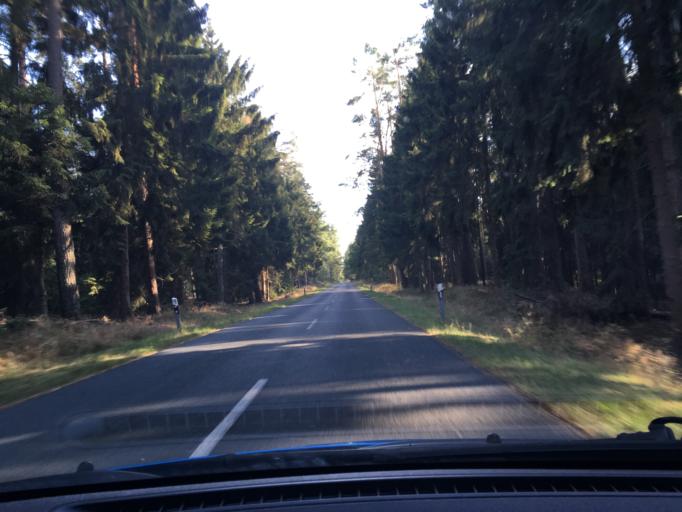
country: DE
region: Lower Saxony
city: Thomasburg
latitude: 53.2440
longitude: 10.7066
